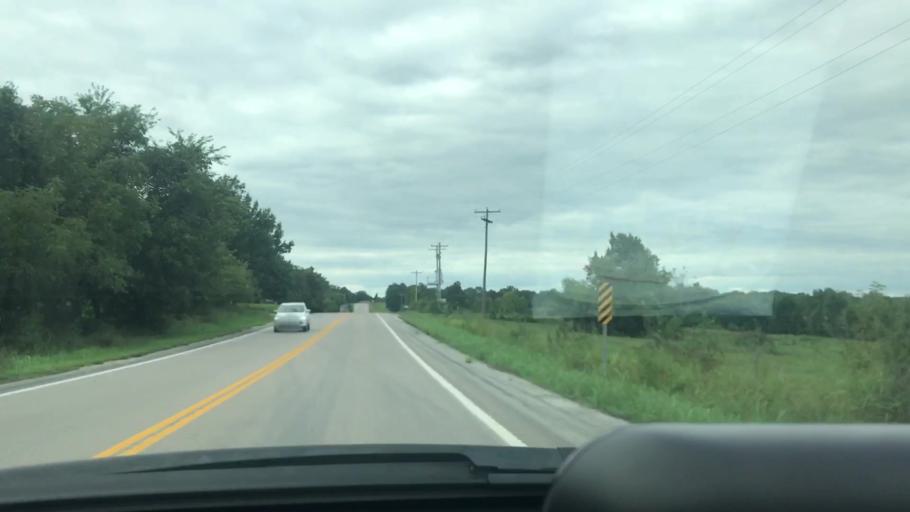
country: US
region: Missouri
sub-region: Benton County
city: Warsaw
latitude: 38.1477
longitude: -93.2919
